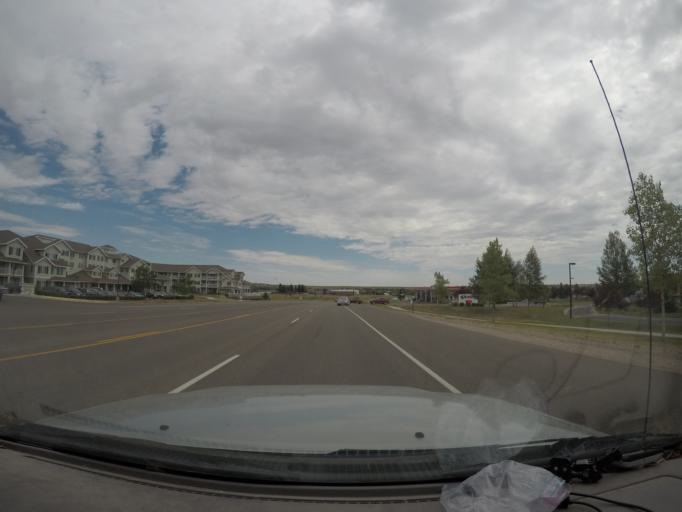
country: US
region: Wyoming
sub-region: Laramie County
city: Fox Farm-College
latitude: 41.1438
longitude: -104.7575
